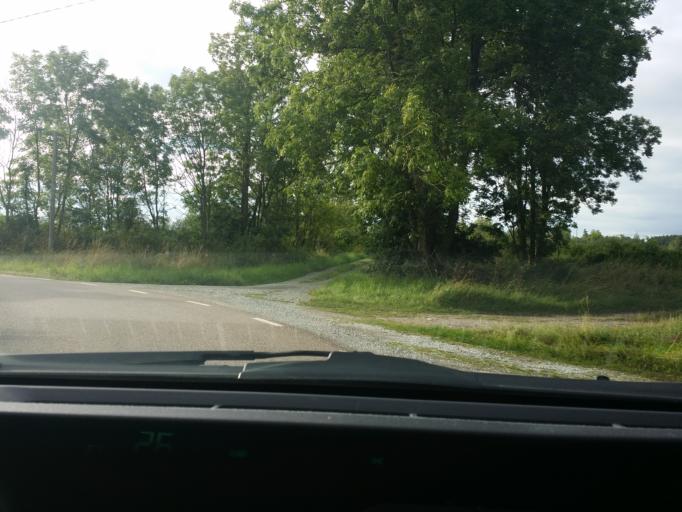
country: SE
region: Kalmar
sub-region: Borgholms Kommun
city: Borgholm
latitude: 57.1117
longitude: 16.9857
